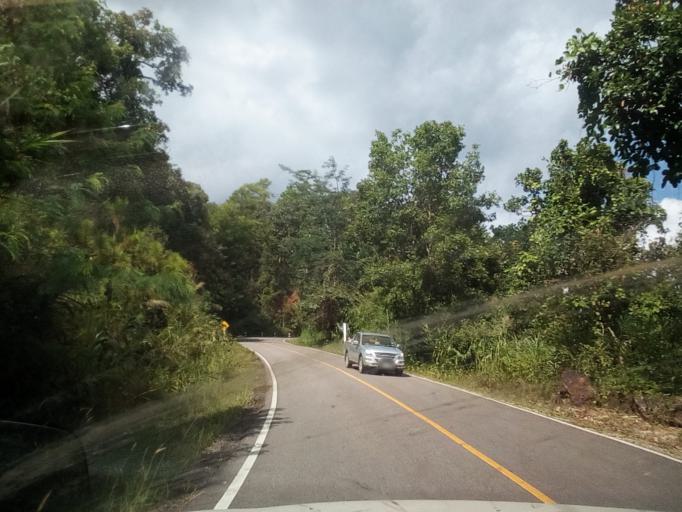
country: TH
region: Chiang Mai
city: Samoeng
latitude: 18.9039
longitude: 98.6752
